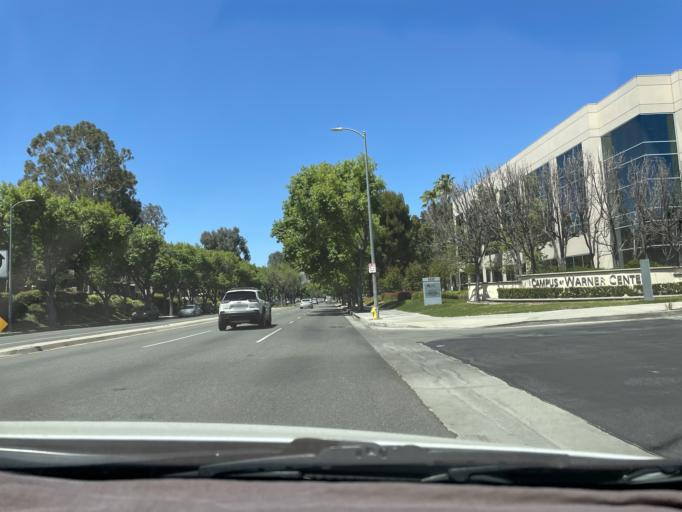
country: US
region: California
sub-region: Los Angeles County
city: Woodland Hills
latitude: 34.1751
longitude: -118.5974
